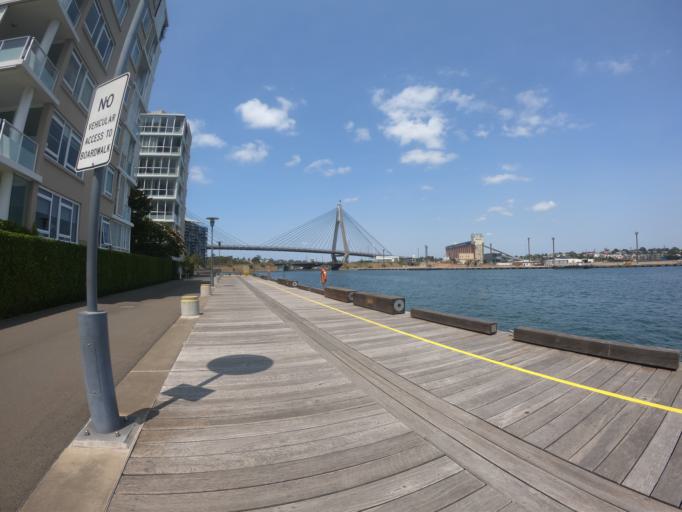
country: AU
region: New South Wales
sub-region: Leichhardt
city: Balmain East
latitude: -33.8661
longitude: 151.1891
